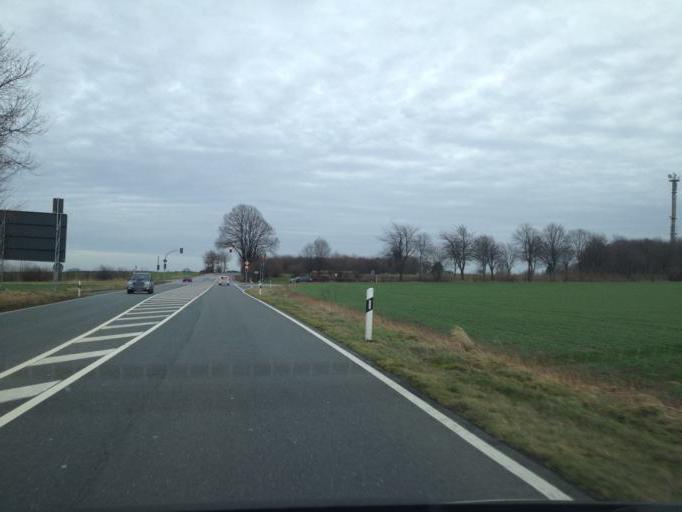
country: DE
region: North Rhine-Westphalia
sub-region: Regierungsbezirk Arnsberg
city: Mohnesee
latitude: 51.5046
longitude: 8.1202
